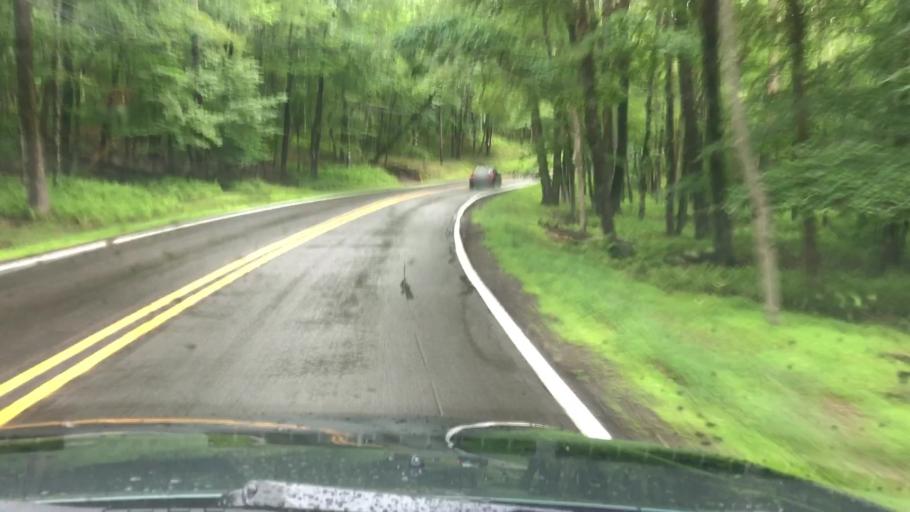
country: US
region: Pennsylvania
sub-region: Monroe County
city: Mountainhome
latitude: 41.2468
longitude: -75.2356
